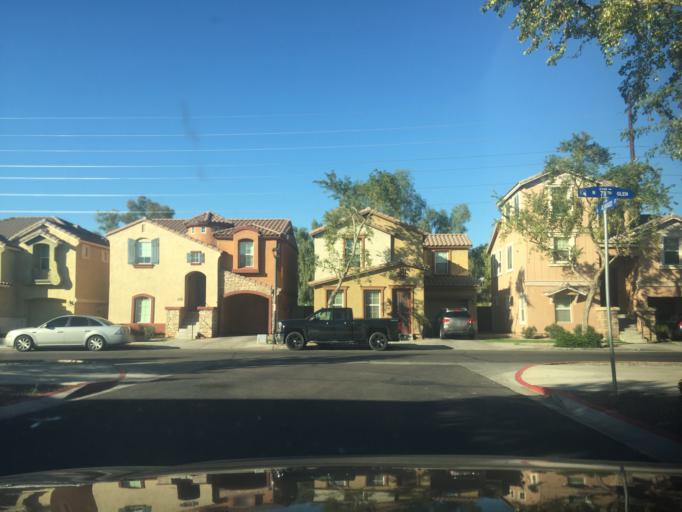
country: US
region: Arizona
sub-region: Maricopa County
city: Tolleson
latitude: 33.4713
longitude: -112.2285
